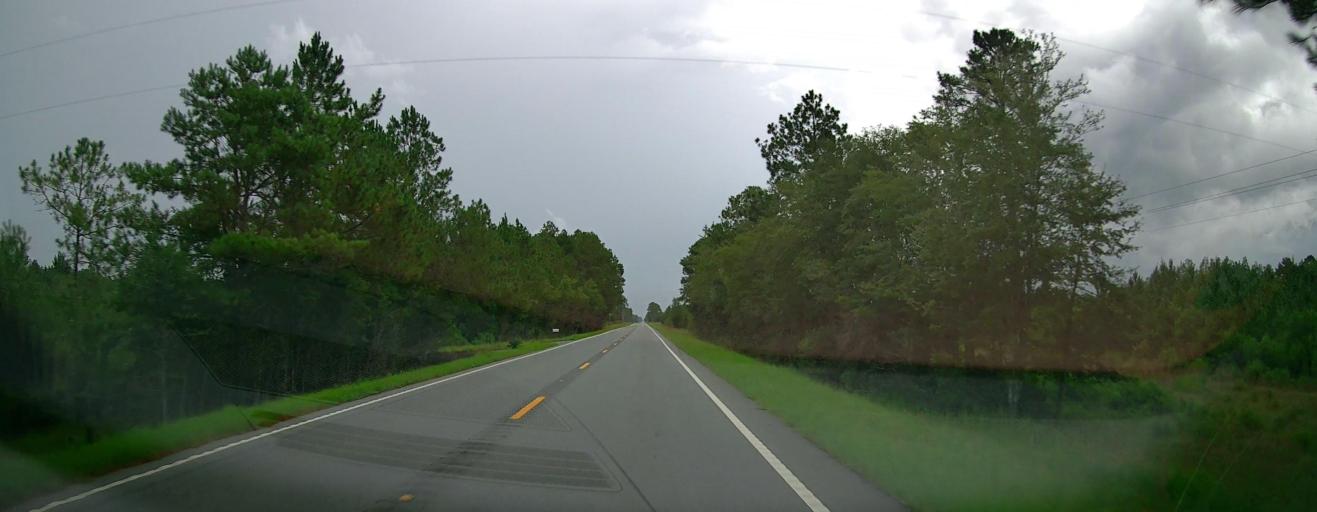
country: US
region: Georgia
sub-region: Brantley County
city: Nahunta
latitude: 31.3472
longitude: -82.0145
